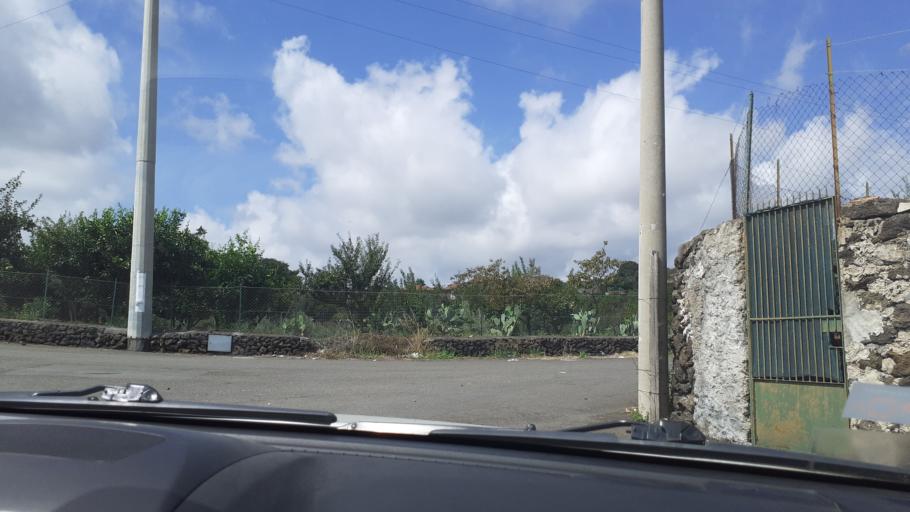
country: IT
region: Sicily
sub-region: Catania
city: Trecastagni
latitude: 37.5959
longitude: 15.0778
